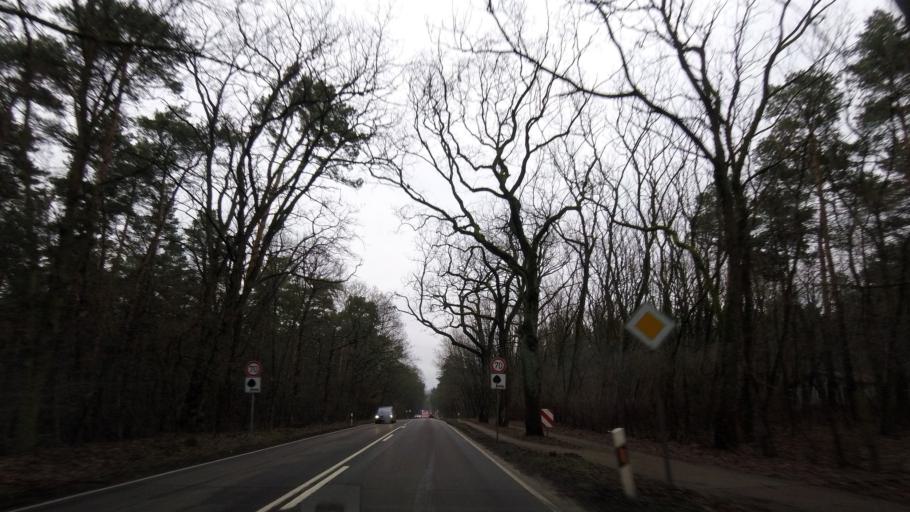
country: DE
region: Brandenburg
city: Beelitz
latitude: 52.2620
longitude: 12.9940
